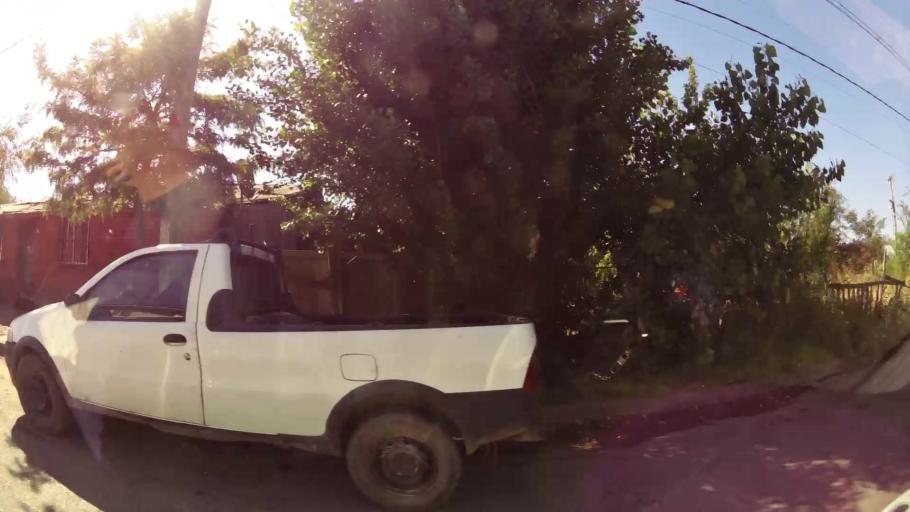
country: CL
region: Maule
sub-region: Provincia de Talca
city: Talca
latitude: -35.3980
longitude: -71.6247
